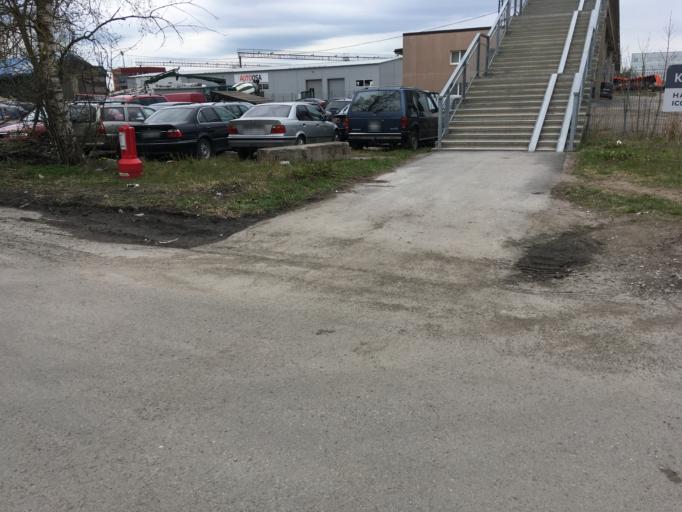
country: EE
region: Harju
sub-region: Tallinna linn
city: Tallinn
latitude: 59.4253
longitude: 24.8183
